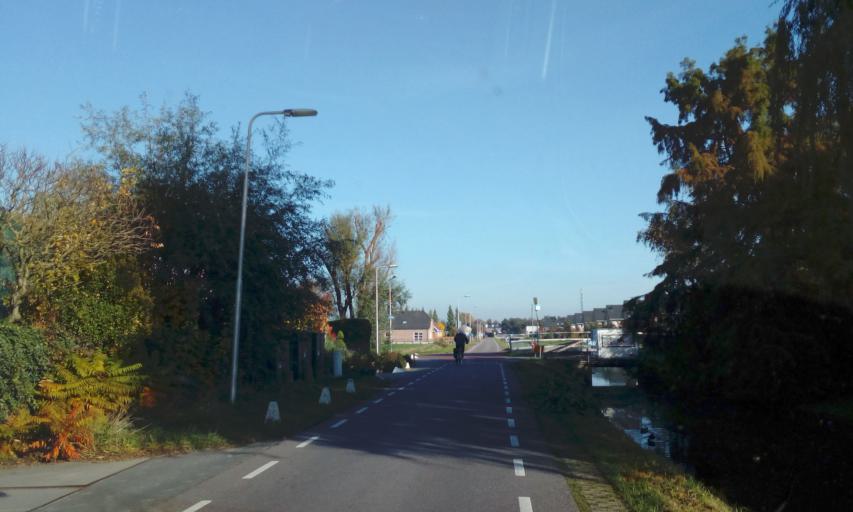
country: NL
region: South Holland
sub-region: Gemeente Lansingerland
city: Berkel en Rodenrijs
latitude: 52.0048
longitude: 4.4754
